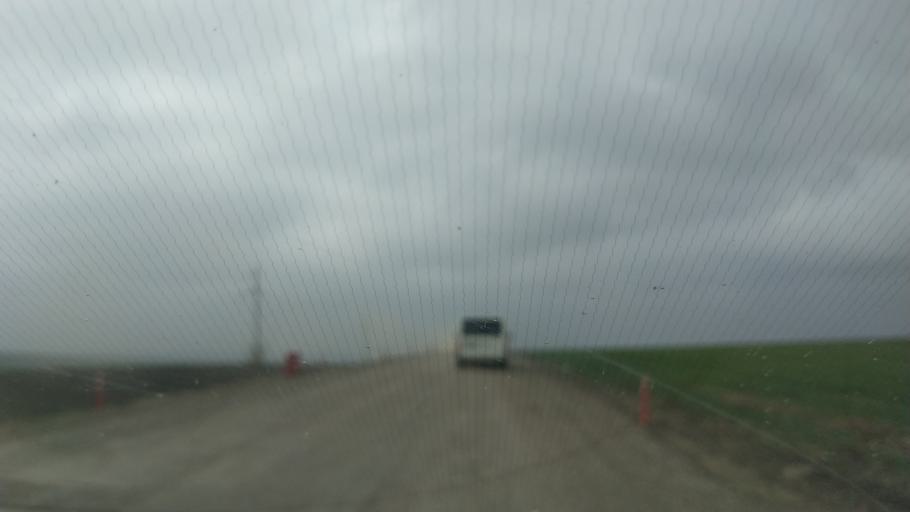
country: MD
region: Gagauzia
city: Comrat
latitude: 46.3240
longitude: 28.7267
